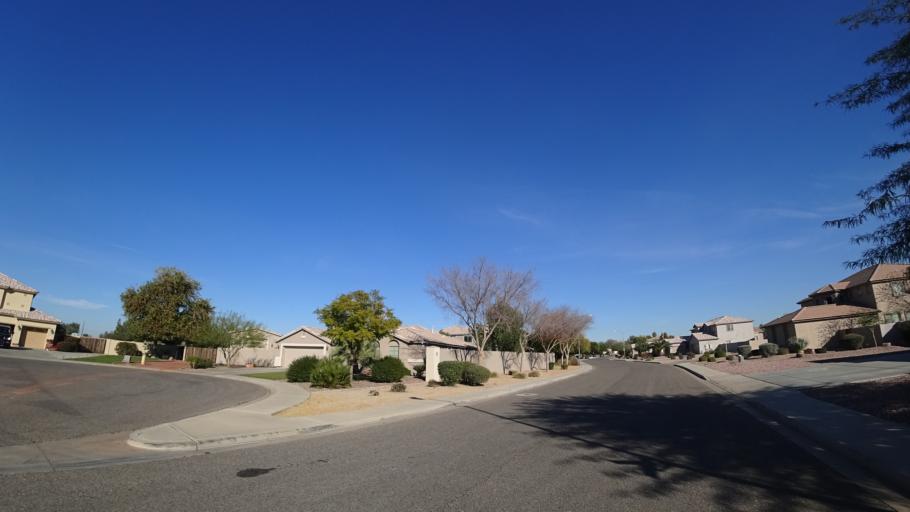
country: US
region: Arizona
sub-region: Maricopa County
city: Glendale
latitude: 33.5189
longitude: -112.2414
